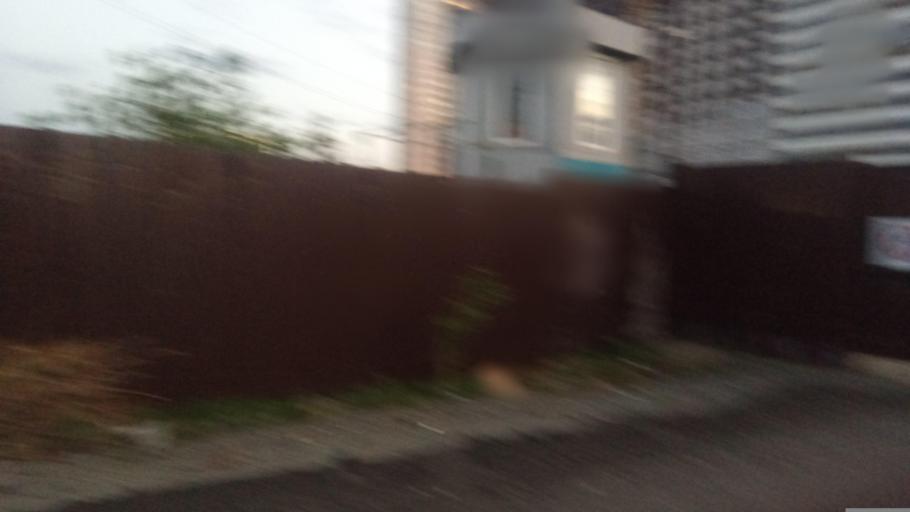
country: RU
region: Chelyabinsk
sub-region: Gorod Chelyabinsk
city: Chelyabinsk
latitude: 55.1712
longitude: 61.3812
